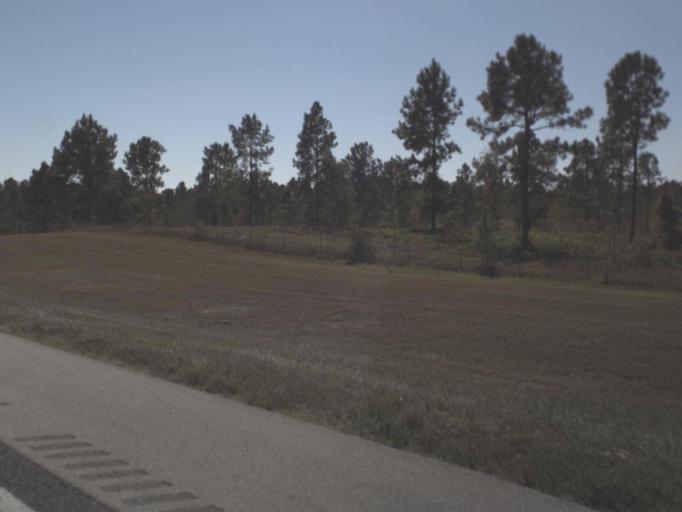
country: US
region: Florida
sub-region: Lake County
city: Minneola
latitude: 28.5930
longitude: -81.7142
